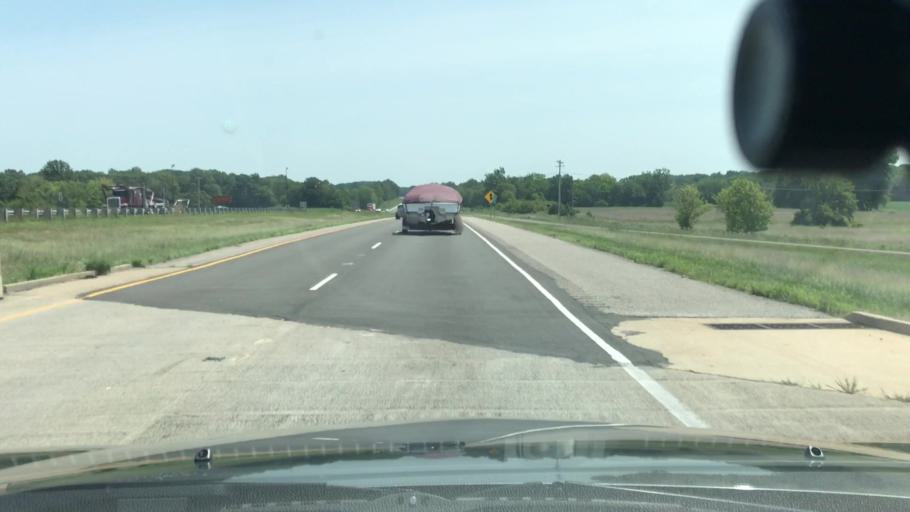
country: US
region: Illinois
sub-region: Clinton County
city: Wamac
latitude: 38.3893
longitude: -89.1703
